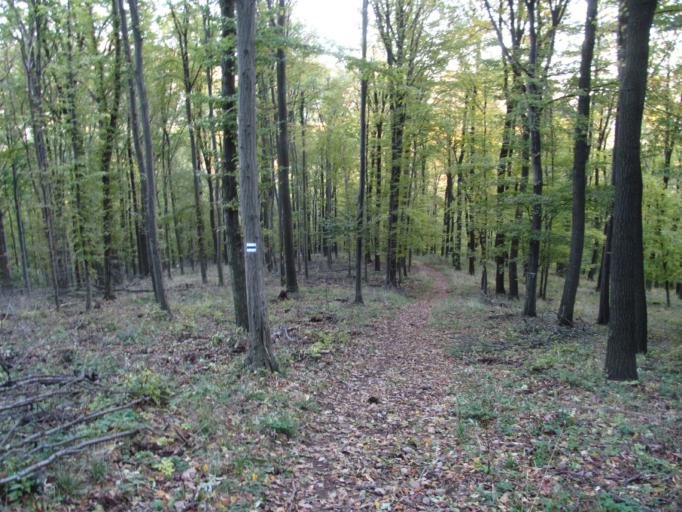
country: HU
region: Heves
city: Paradsasvar
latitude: 47.8917
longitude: 19.9727
